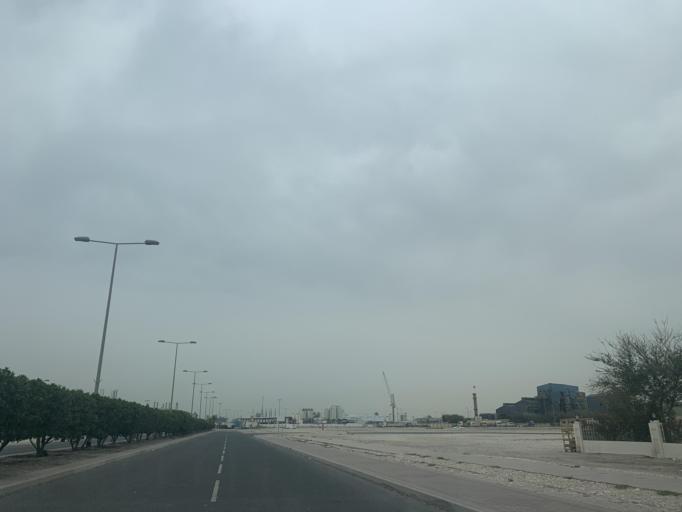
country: BH
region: Muharraq
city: Al Hadd
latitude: 26.2127
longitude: 50.6729
